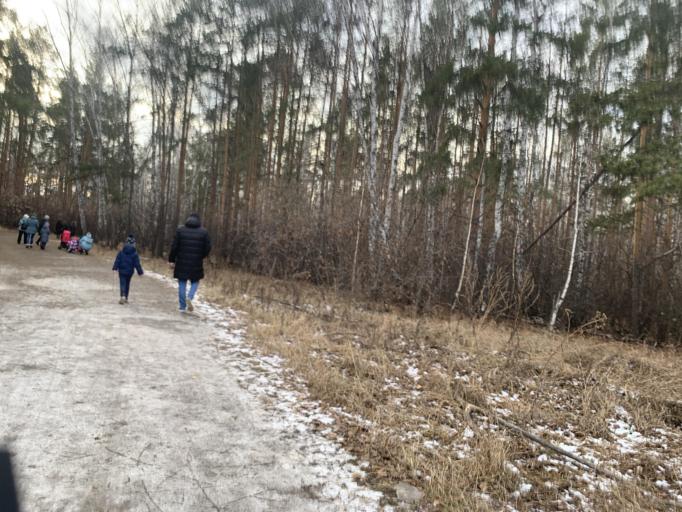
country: RU
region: Chelyabinsk
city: Roshchino
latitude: 55.1989
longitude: 61.3008
